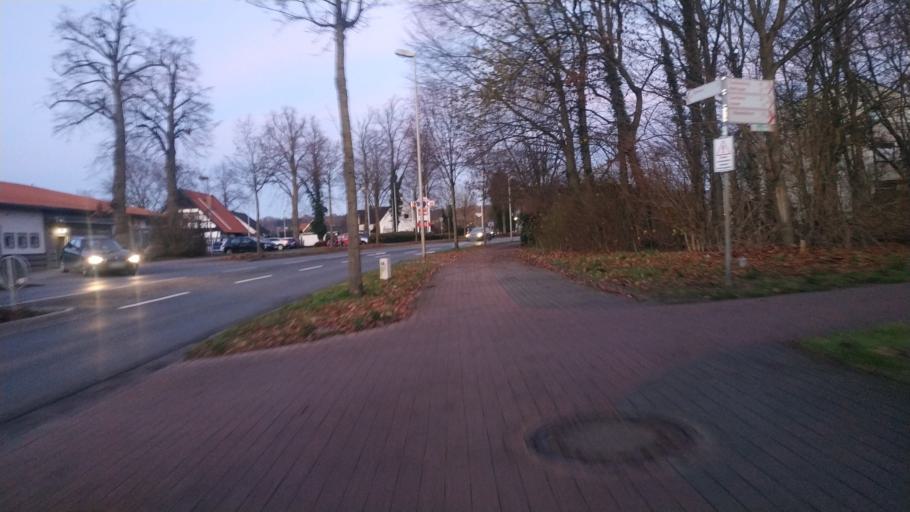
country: DE
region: North Rhine-Westphalia
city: Ibbenburen
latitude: 52.2748
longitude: 7.6955
